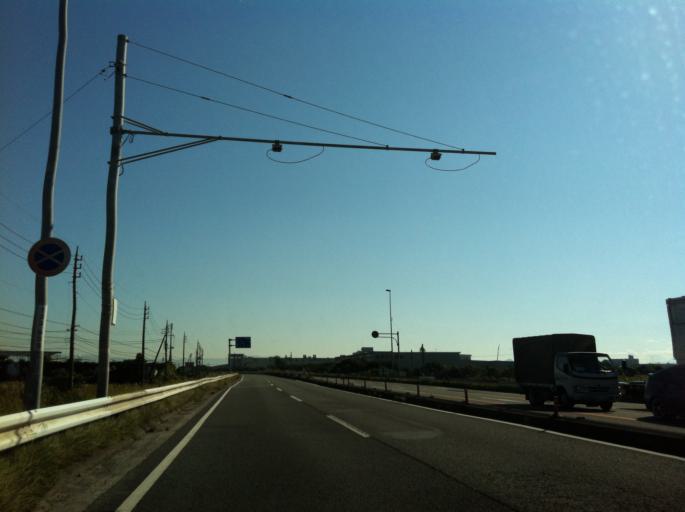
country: JP
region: Shizuoka
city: Fuji
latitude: 35.1345
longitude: 138.7751
